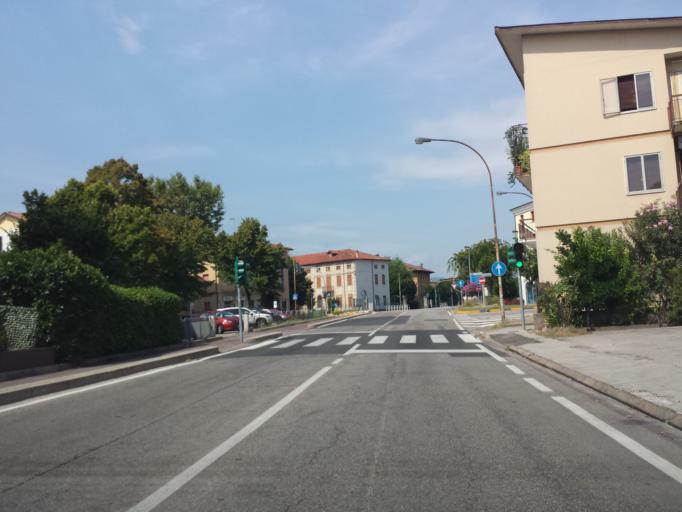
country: IT
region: Veneto
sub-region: Provincia di Vicenza
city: Montecchio Maggiore-Alte Ceccato
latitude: 45.5046
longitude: 11.4066
